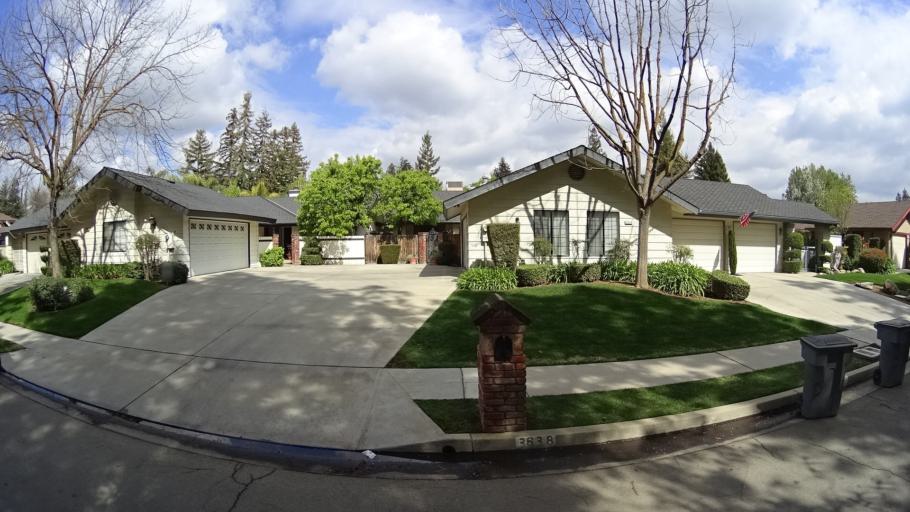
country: US
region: California
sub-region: Fresno County
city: Fresno
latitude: 36.8384
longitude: -119.8589
